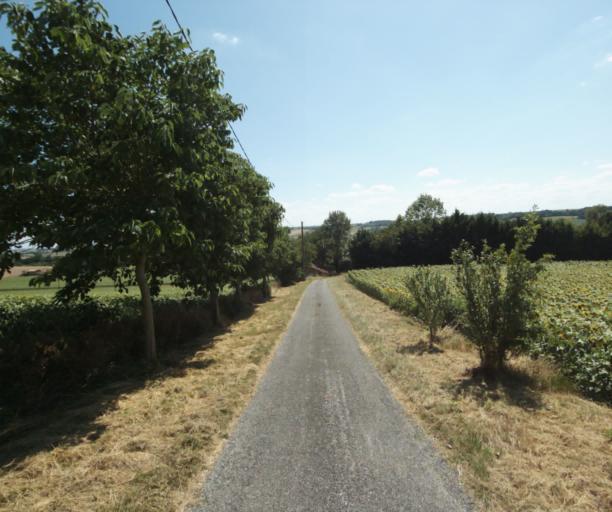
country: FR
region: Midi-Pyrenees
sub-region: Departement de la Haute-Garonne
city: Saint-Felix-Lauragais
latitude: 43.4988
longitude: 1.8804
